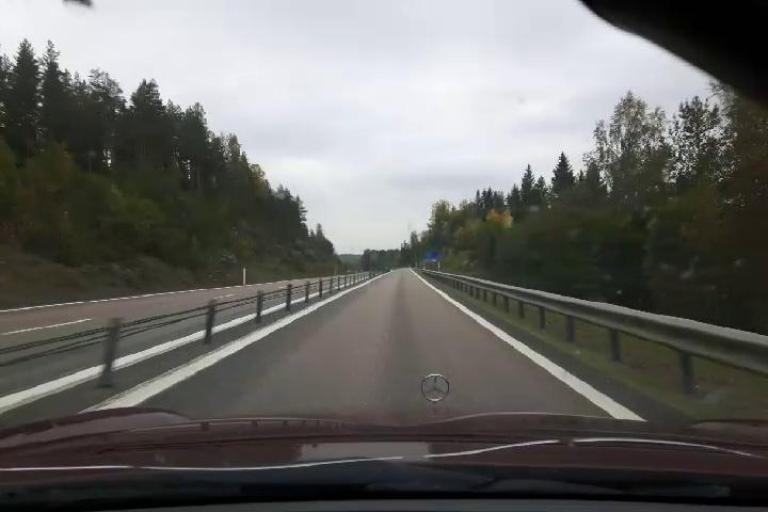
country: SE
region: Vaesternorrland
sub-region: Kramfors Kommun
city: Nordingra
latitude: 62.9360
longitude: 18.0936
